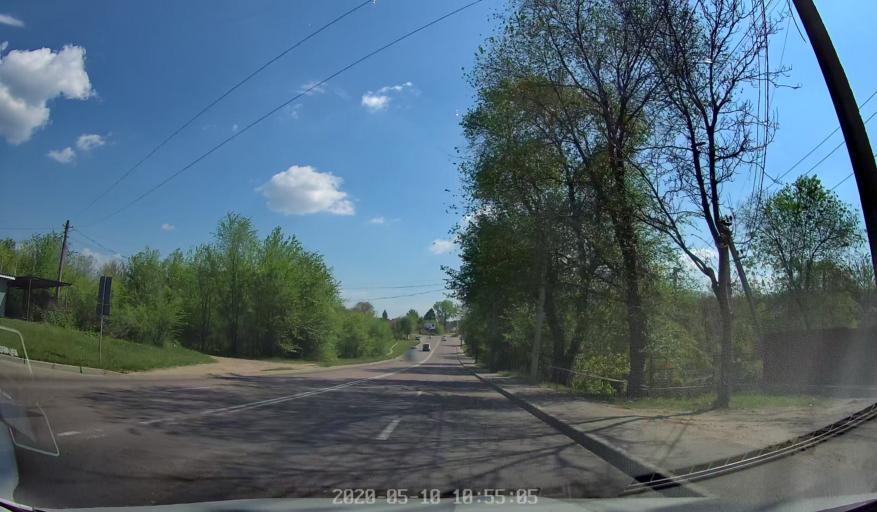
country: MD
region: Chisinau
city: Chisinau
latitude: 47.0368
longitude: 28.9010
